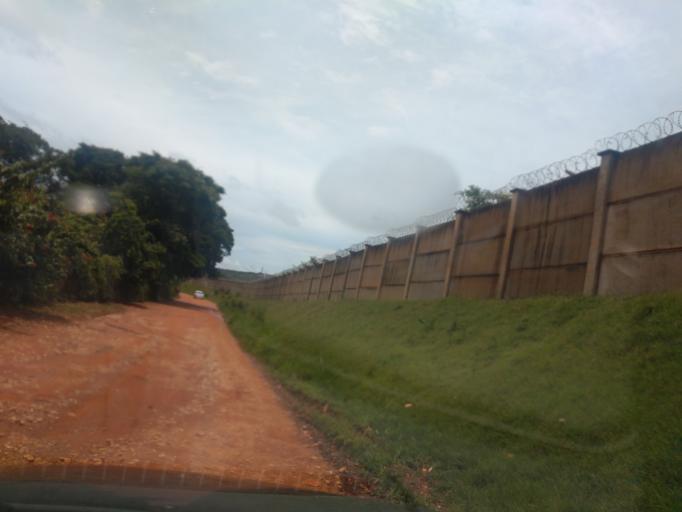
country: BR
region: Minas Gerais
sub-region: Tres Coracoes
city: Tres Coracoes
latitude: -21.6774
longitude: -45.2568
